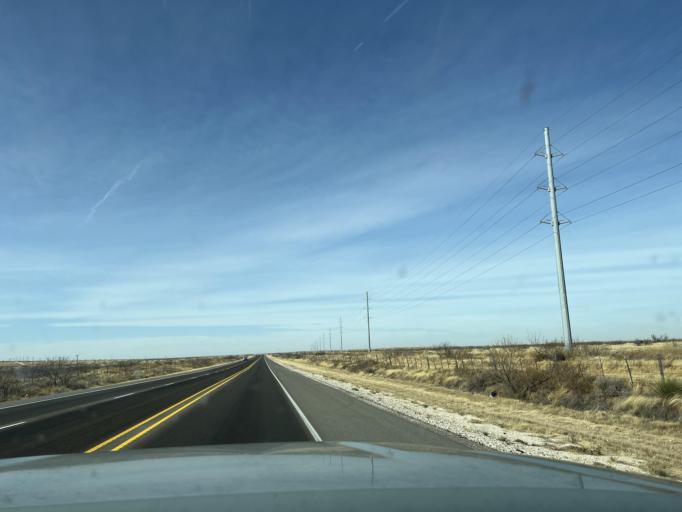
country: US
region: Texas
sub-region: Andrews County
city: Andrews
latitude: 32.3537
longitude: -102.7506
